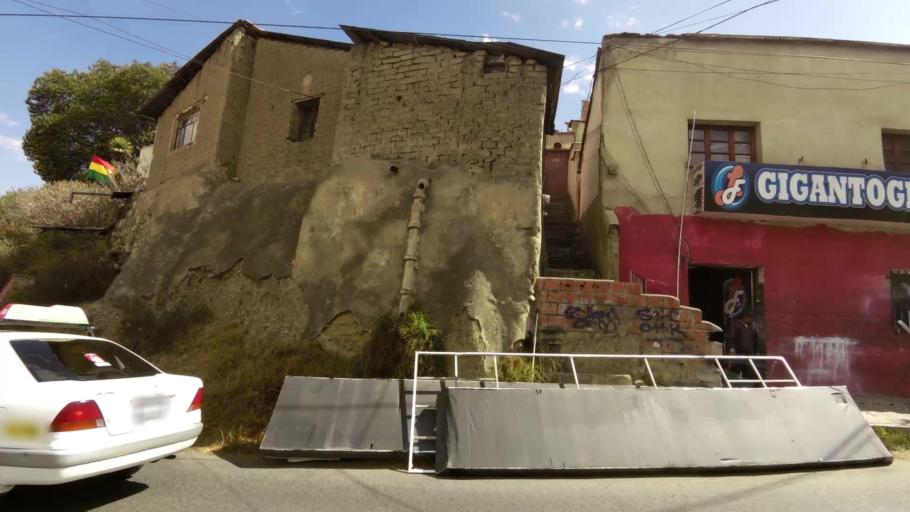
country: BO
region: La Paz
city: La Paz
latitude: -16.4931
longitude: -68.1249
